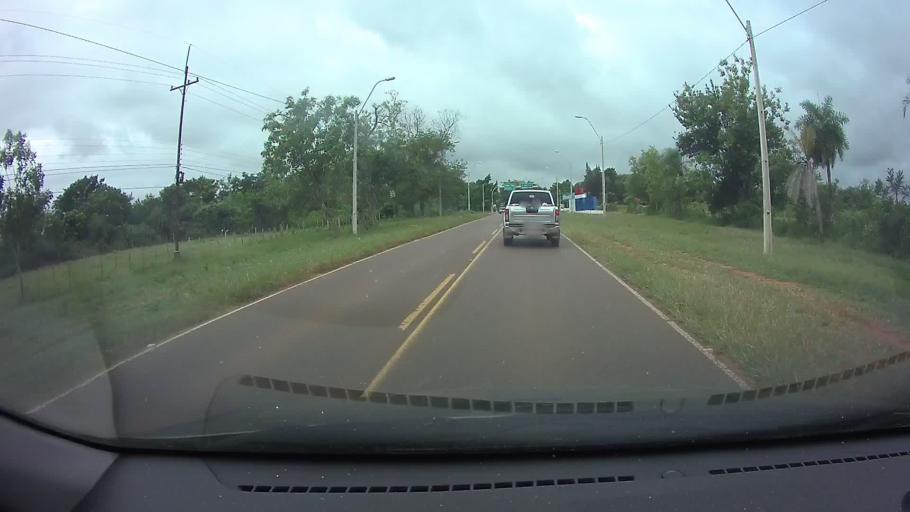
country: PY
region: Central
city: Nueva Italia
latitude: -25.6098
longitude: -57.4740
